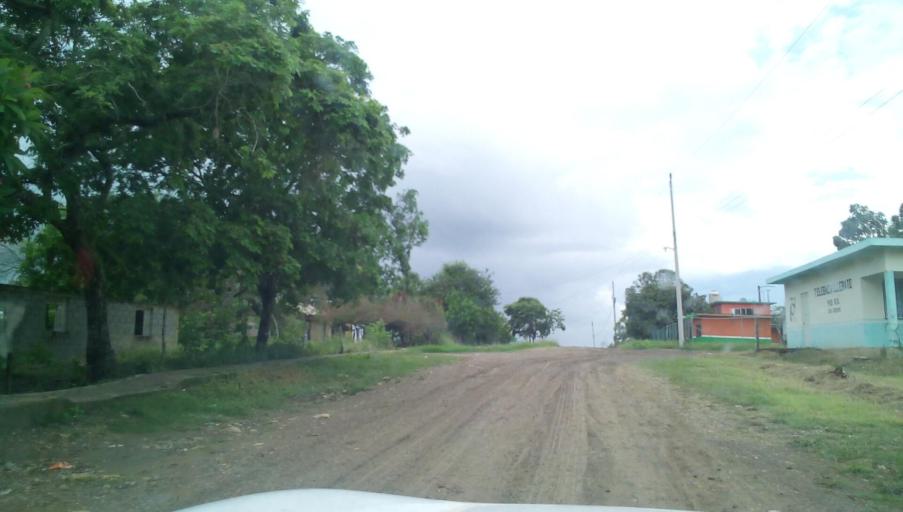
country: MX
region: Veracruz
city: Panuco
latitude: 21.8016
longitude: -98.1062
